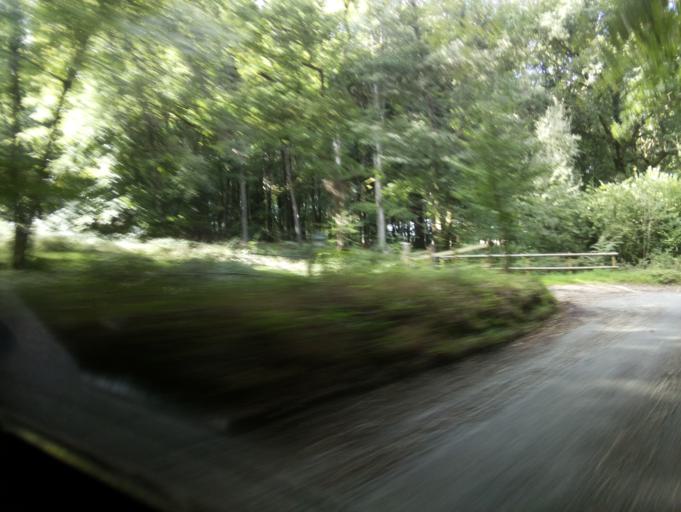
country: GB
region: England
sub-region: Hampshire
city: Chandlers Ford
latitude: 51.0665
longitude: -1.3791
